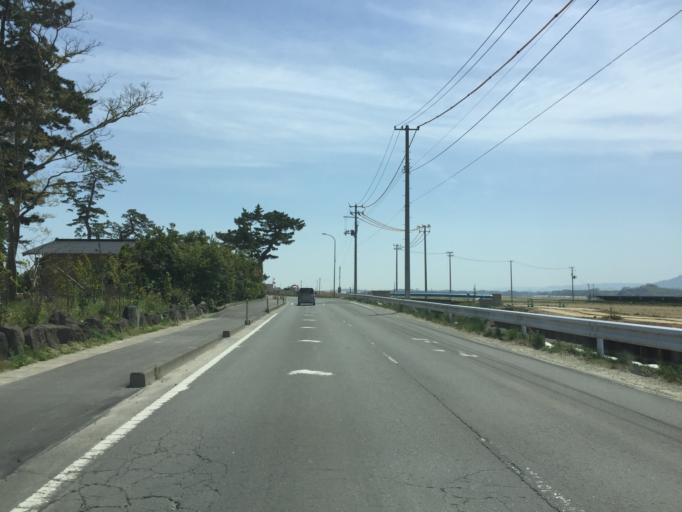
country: JP
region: Miyagi
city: Watari
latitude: 37.9573
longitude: 140.9098
